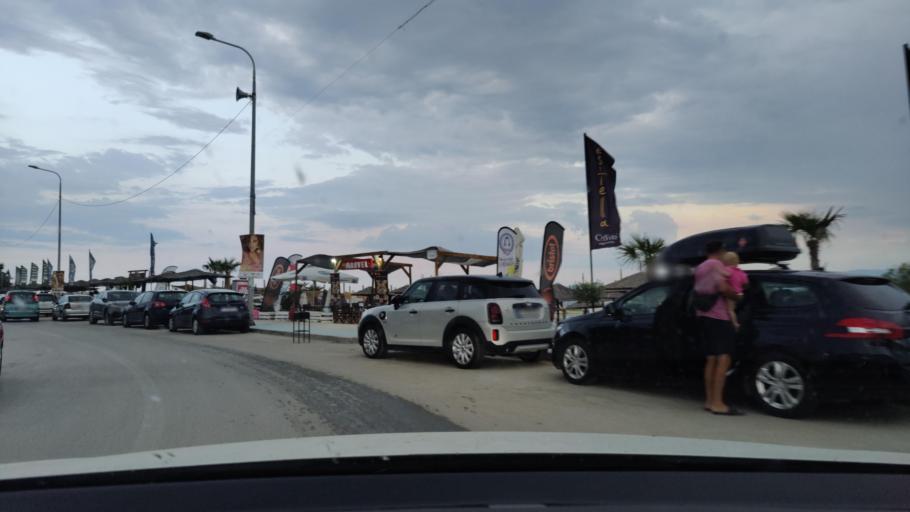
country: GR
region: East Macedonia and Thrace
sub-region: Nomos Kavalas
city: Paralia Ofryniou
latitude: 40.7651
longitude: 23.8996
